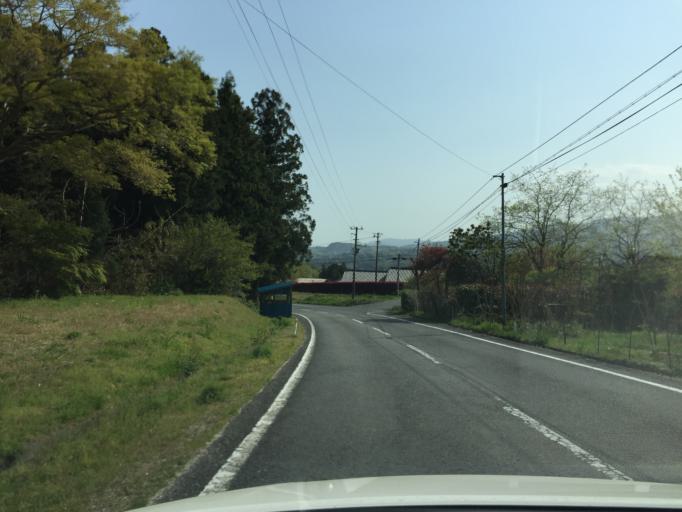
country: JP
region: Fukushima
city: Iwaki
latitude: 37.1504
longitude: 140.8587
